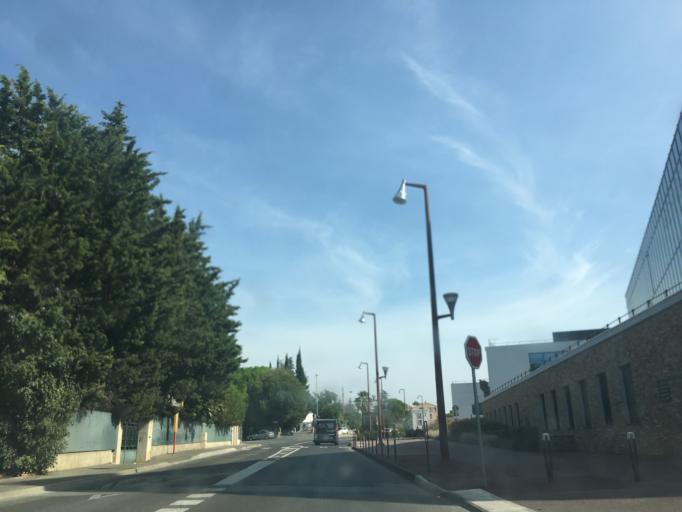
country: FR
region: Provence-Alpes-Cote d'Azur
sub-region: Departement du Var
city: Draguignan
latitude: 43.5356
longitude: 6.4748
